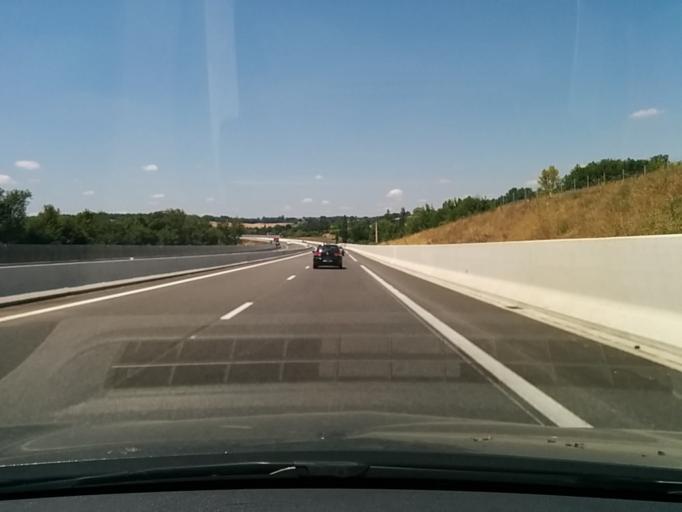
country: FR
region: Midi-Pyrenees
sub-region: Departement du Gers
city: Preignan
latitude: 43.6562
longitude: 0.6636
